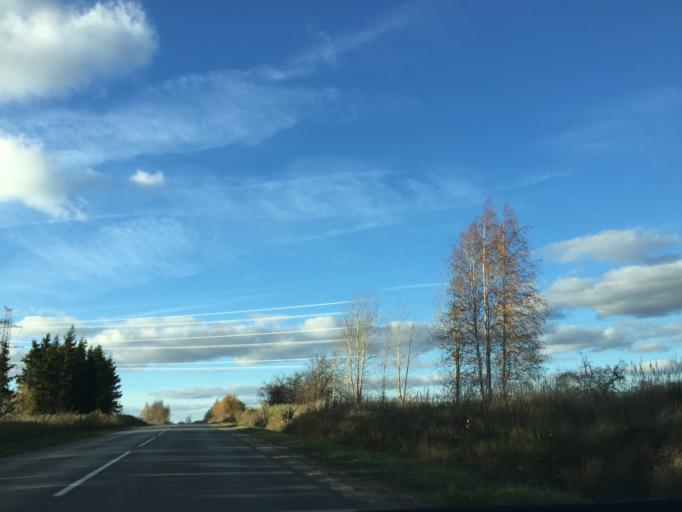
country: LV
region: Tukuma Rajons
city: Tukums
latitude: 56.9819
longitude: 23.1122
